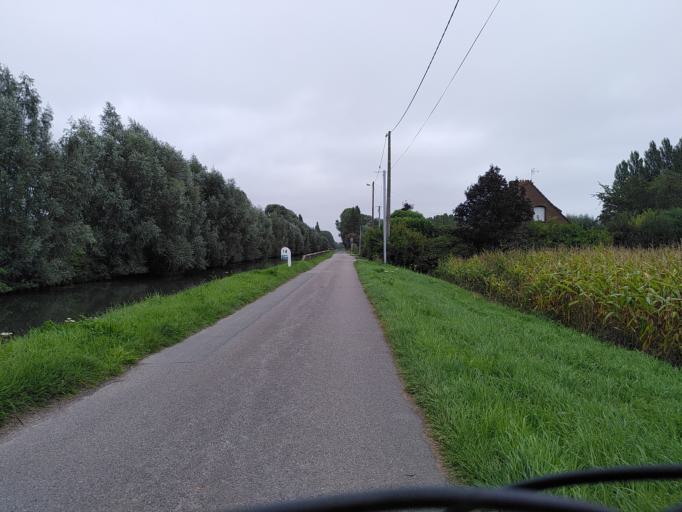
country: FR
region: Nord-Pas-de-Calais
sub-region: Departement du Nord
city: Haverskerque
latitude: 50.6309
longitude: 2.5670
